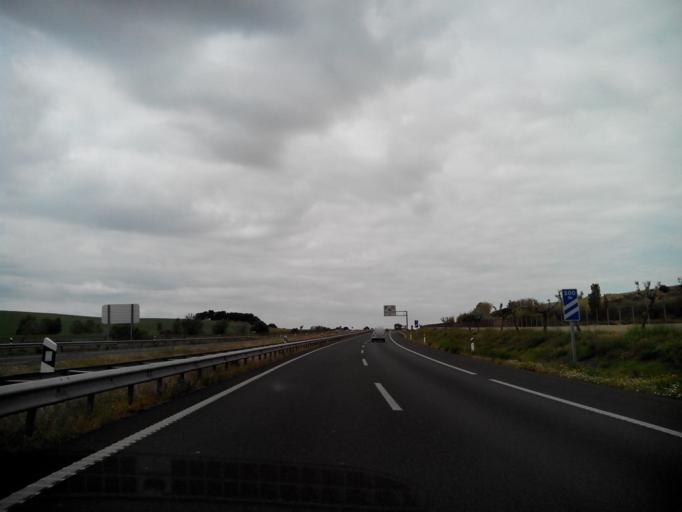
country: ES
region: Catalonia
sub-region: Provincia de Lleida
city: Bellpuig
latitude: 41.6345
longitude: 1.0429
